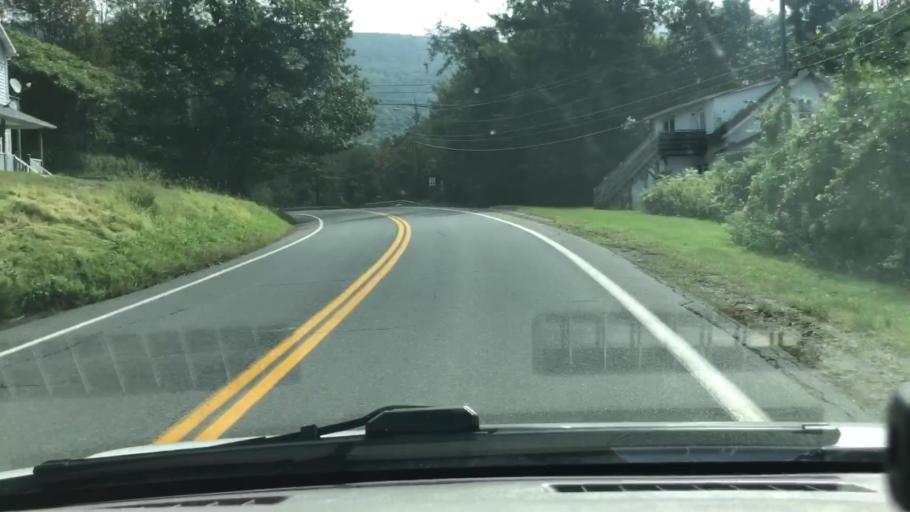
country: US
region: Massachusetts
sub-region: Berkshire County
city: North Adams
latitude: 42.6903
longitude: -73.0841
